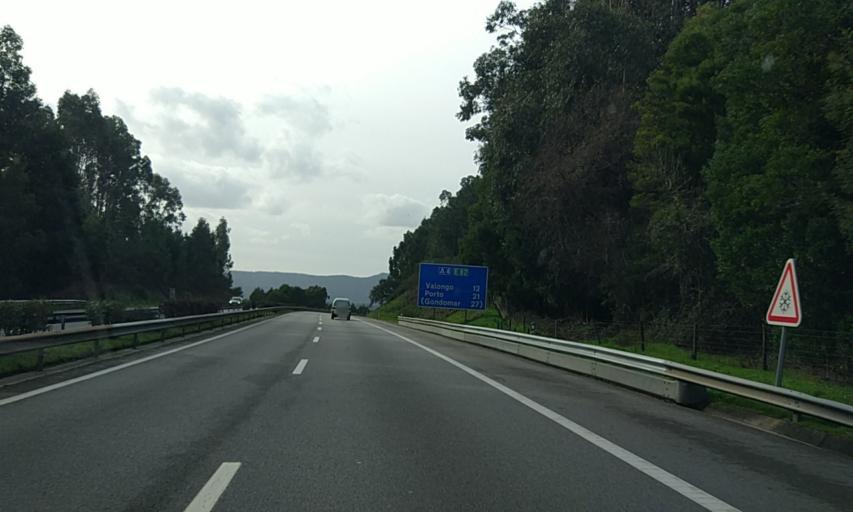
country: PT
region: Porto
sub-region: Paredes
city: Recarei
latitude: 41.1672
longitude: -8.3926
